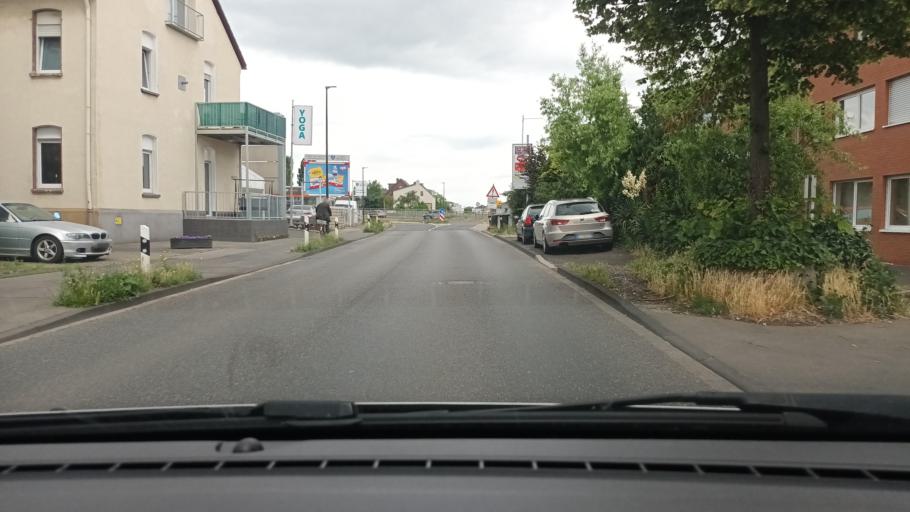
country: DE
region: North Rhine-Westphalia
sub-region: Regierungsbezirk Koln
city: Hurth
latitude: 50.8734
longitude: 6.8912
